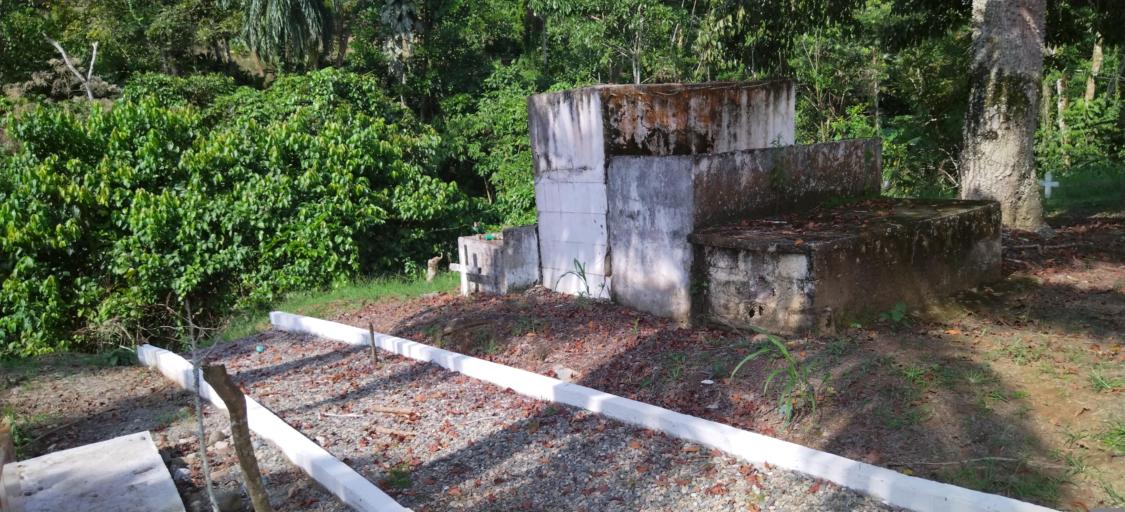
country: EC
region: Napo
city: Tena
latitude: -1.0405
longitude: -77.7903
